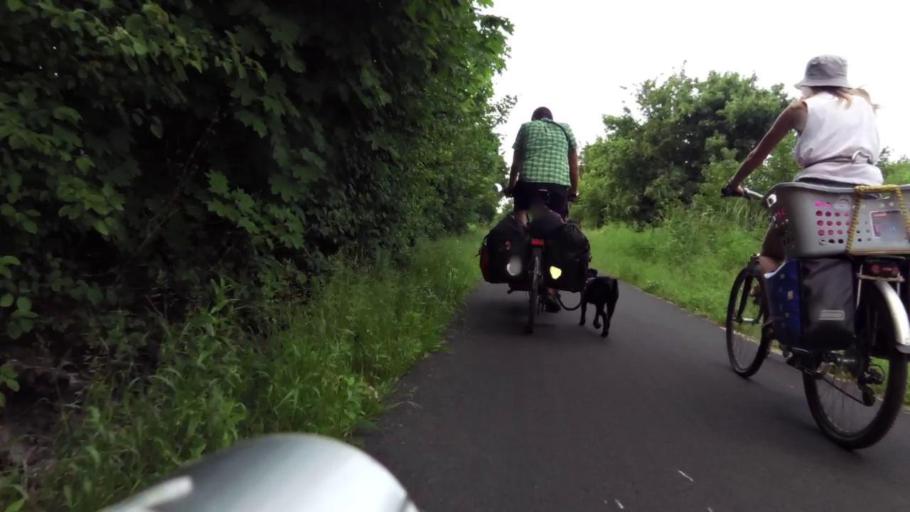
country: PL
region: Kujawsko-Pomorskie
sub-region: Powiat torunski
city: Lubianka
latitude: 53.0964
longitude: 18.5316
